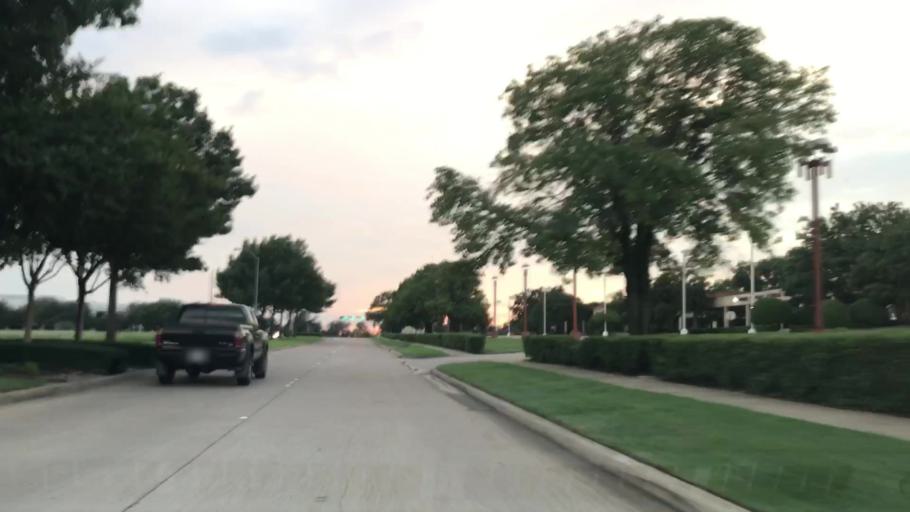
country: US
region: Texas
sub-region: Dallas County
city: Addison
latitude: 33.0191
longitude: -96.8411
